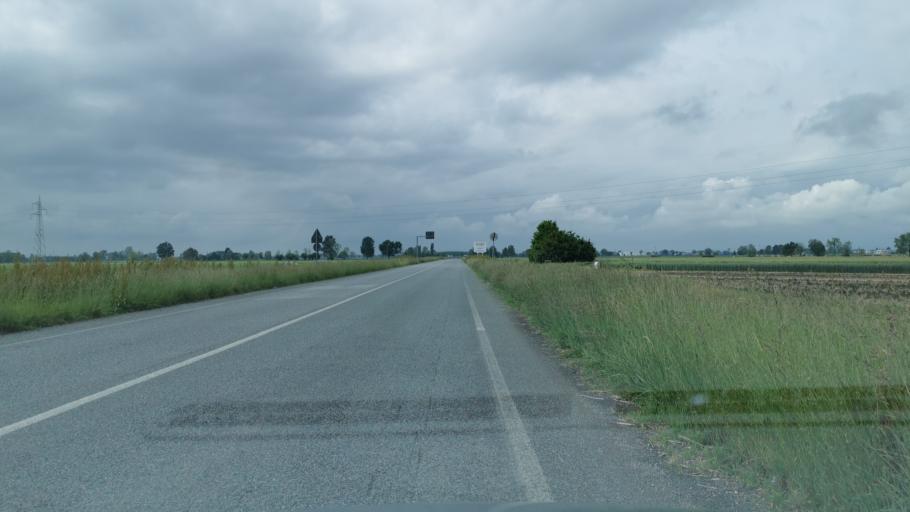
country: IT
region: Piedmont
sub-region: Provincia di Cuneo
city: Racconigi
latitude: 44.7625
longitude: 7.6973
